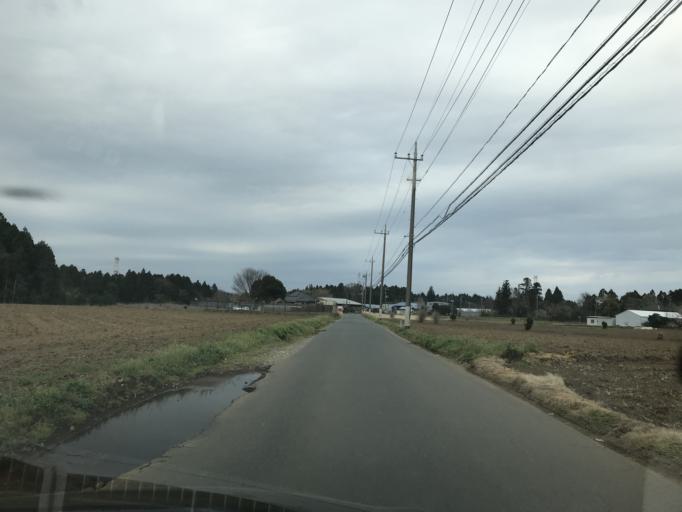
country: JP
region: Chiba
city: Sawara
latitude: 35.8400
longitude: 140.4933
